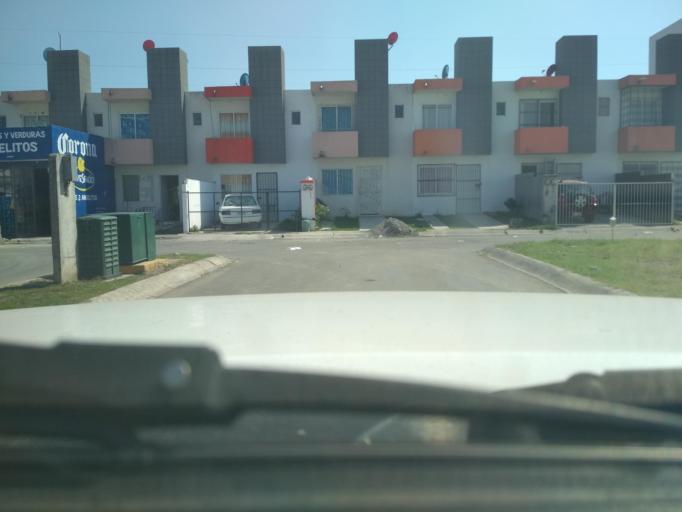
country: MX
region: Veracruz
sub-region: Veracruz
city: Las Amapolas
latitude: 19.1566
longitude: -96.2228
